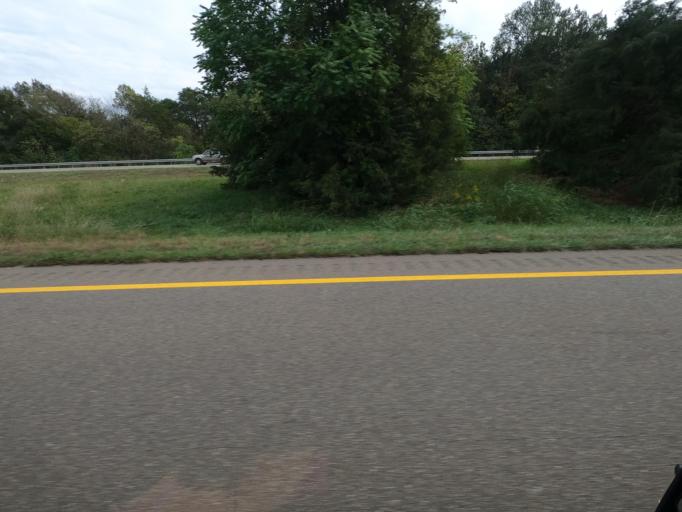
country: US
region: Tennessee
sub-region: Hamblen County
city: Morristown
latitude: 36.1755
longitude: -83.2069
